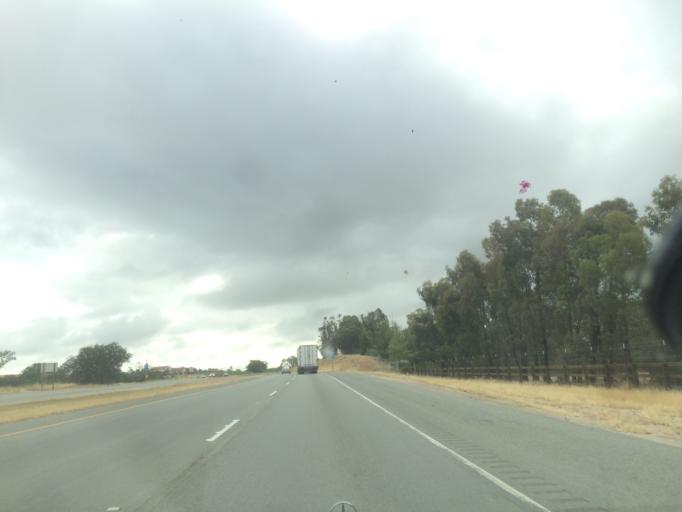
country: US
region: California
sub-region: San Luis Obispo County
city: Paso Robles
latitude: 35.6444
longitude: -120.6400
